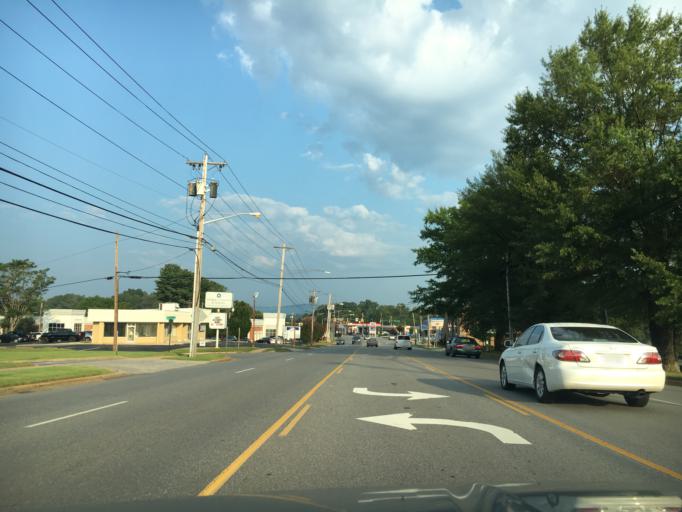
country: US
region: Virginia
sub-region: City of Lynchburg
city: West Lynchburg
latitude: 37.4127
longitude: -79.1731
